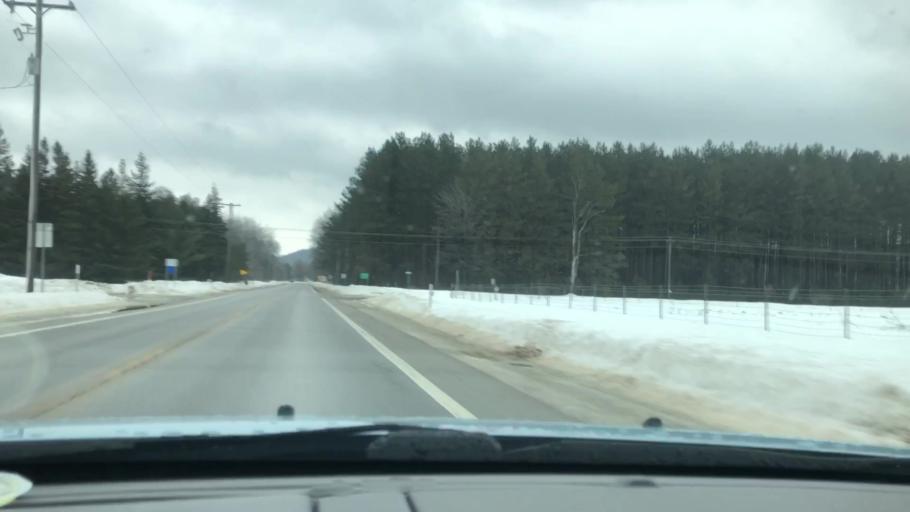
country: US
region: Michigan
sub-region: Charlevoix County
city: East Jordan
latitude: 45.1325
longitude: -85.0998
